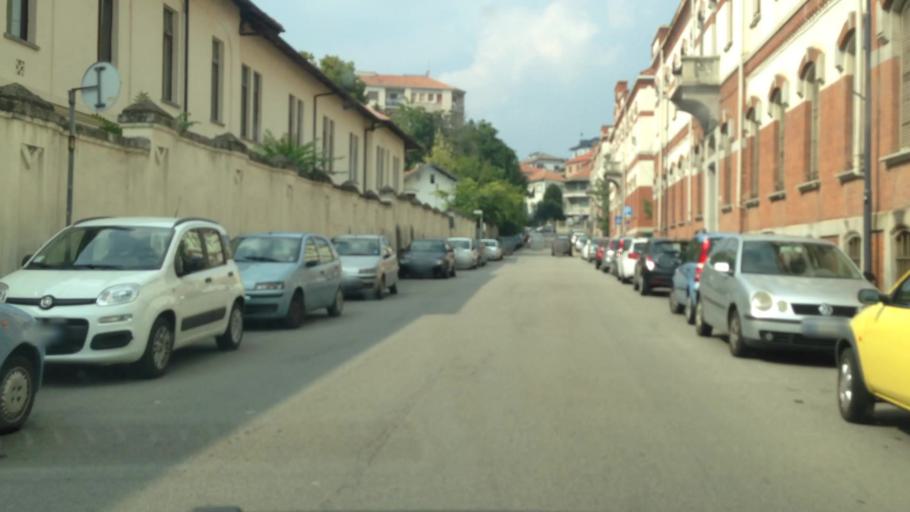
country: IT
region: Piedmont
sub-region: Provincia di Asti
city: Asti
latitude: 44.9035
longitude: 8.2123
